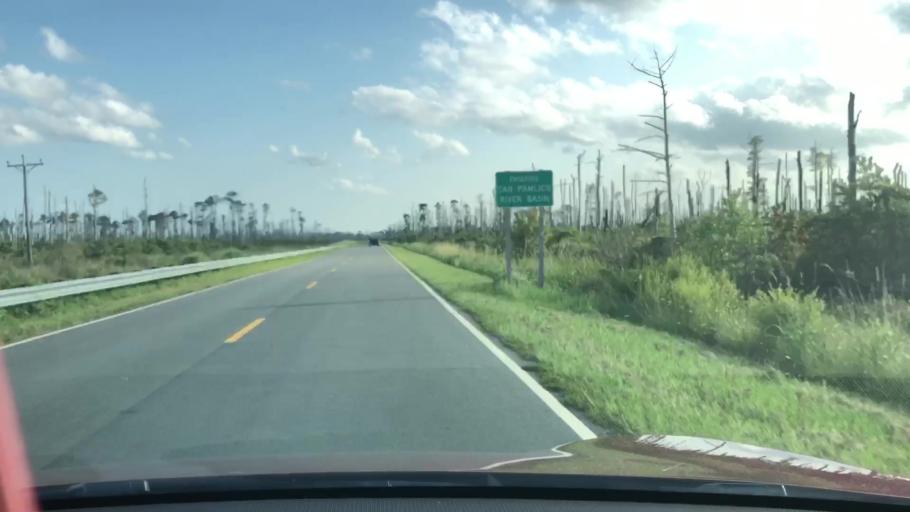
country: US
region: North Carolina
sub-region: Dare County
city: Wanchese
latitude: 35.6404
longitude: -75.7782
